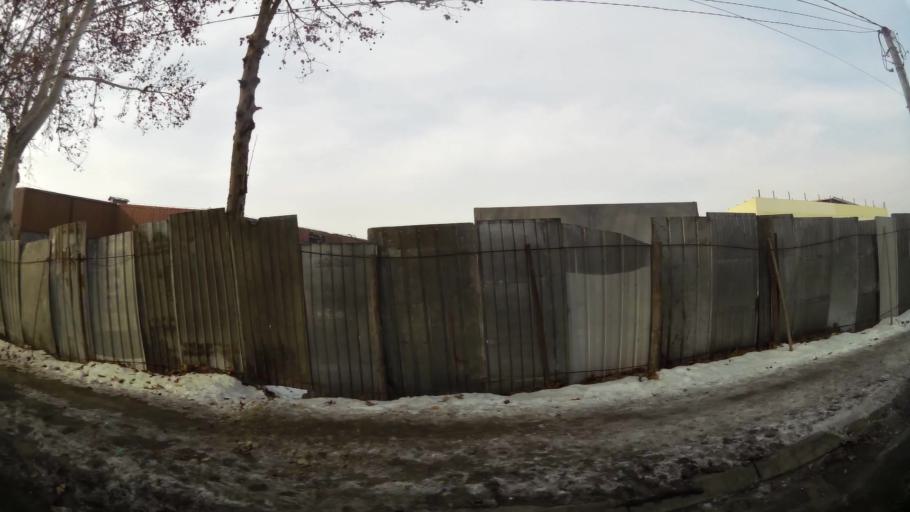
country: MK
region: Cair
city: Cair
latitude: 42.0245
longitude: 21.4299
